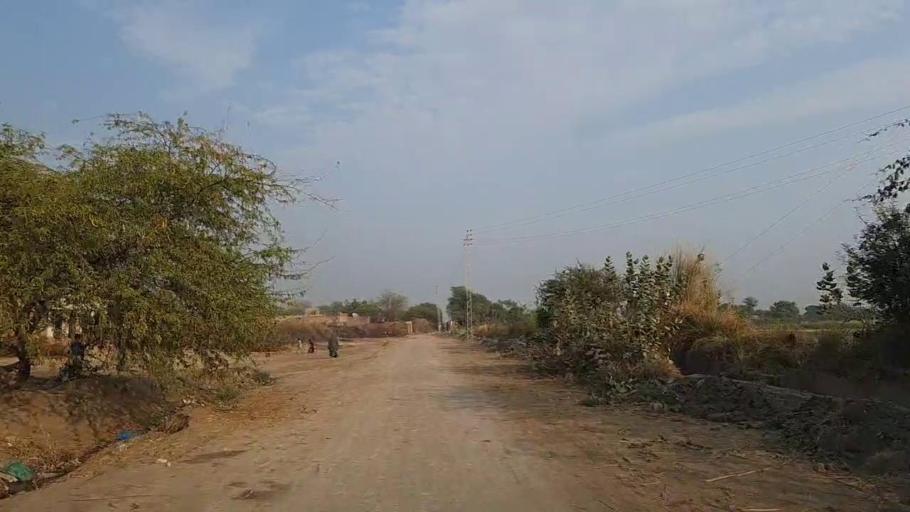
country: PK
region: Sindh
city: Jam Sahib
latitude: 26.3098
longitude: 68.5348
